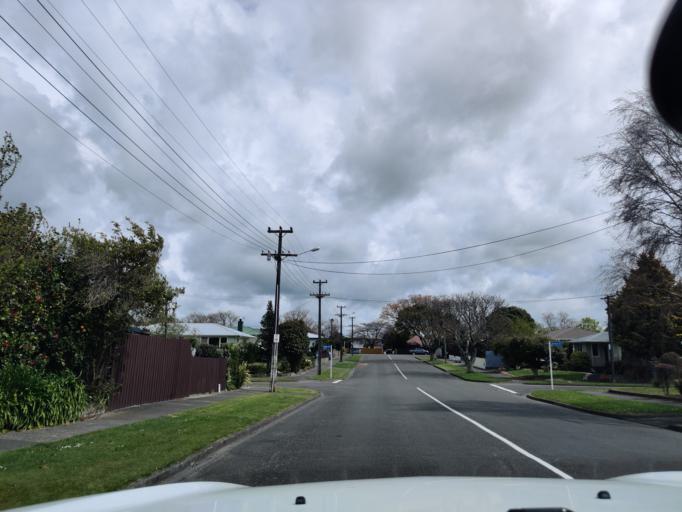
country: NZ
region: Manawatu-Wanganui
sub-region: Palmerston North City
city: Palmerston North
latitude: -40.3806
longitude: 175.5879
